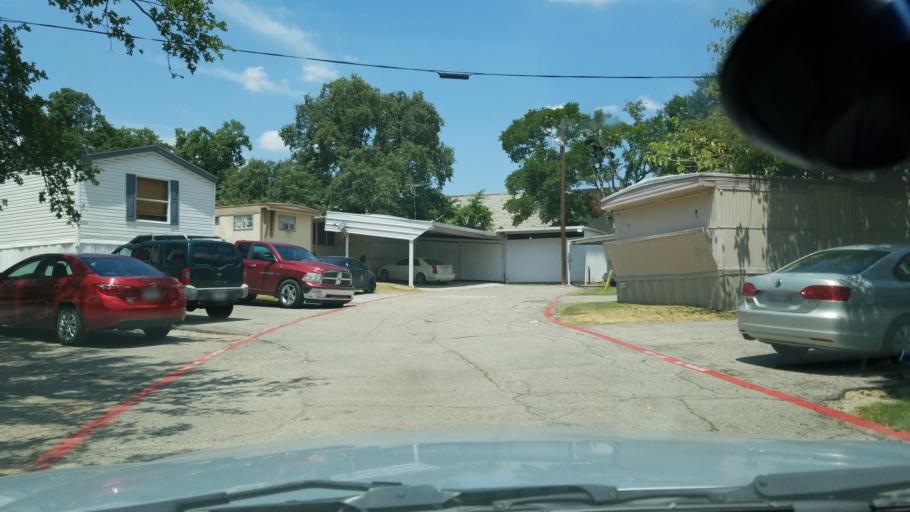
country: US
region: Texas
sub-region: Dallas County
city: Irving
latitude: 32.8270
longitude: -96.9953
